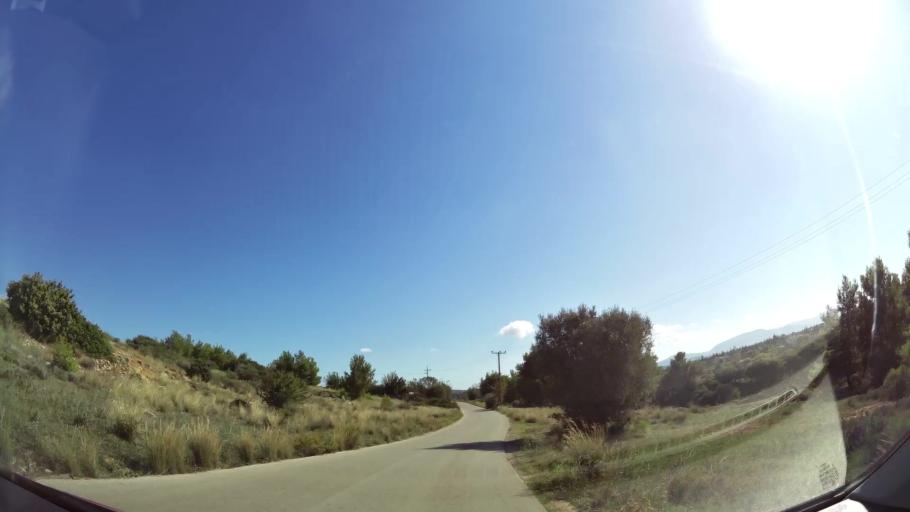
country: GR
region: Attica
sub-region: Nomarchia Anatolikis Attikis
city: Pikermi
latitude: 38.0117
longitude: 23.9378
